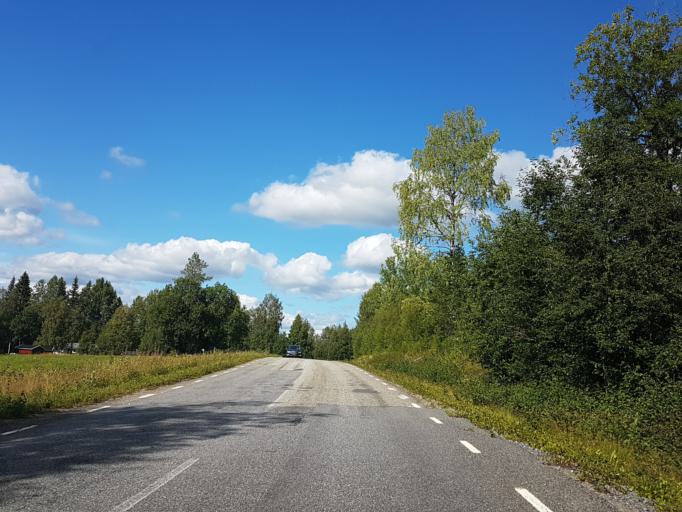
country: SE
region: Vaesterbotten
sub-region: Skelleftea Kommun
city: Burtraesk
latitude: 64.2366
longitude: 20.4787
